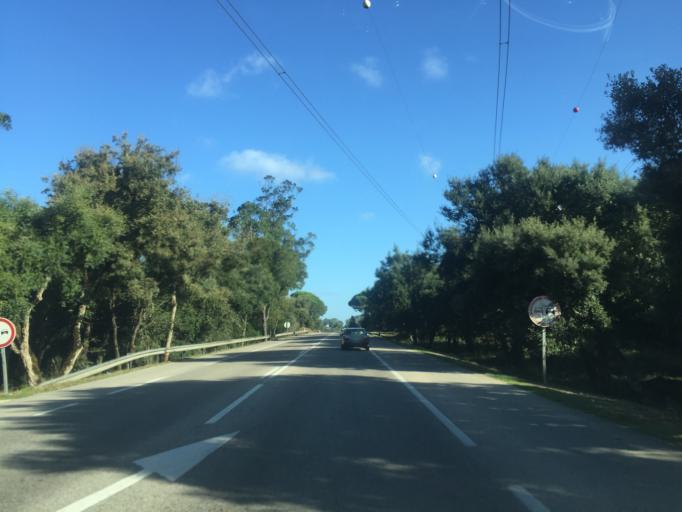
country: PT
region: Leiria
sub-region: Alcobaca
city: Turquel
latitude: 39.4696
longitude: -8.9415
